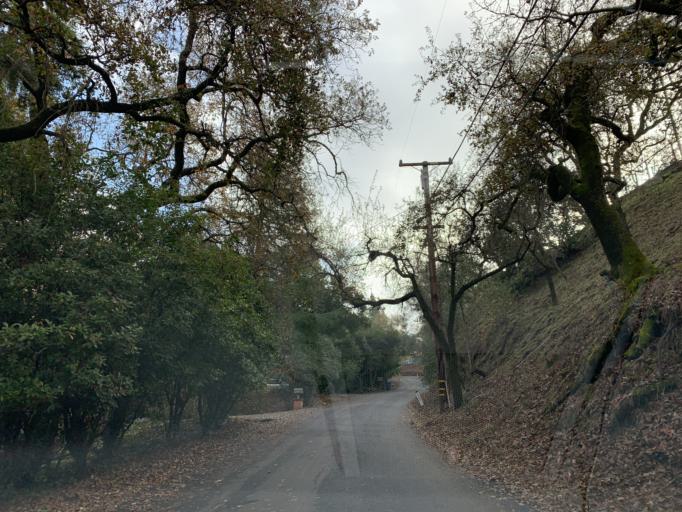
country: US
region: California
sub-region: Contra Costa County
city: Saranap
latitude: 37.8829
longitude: -122.0747
